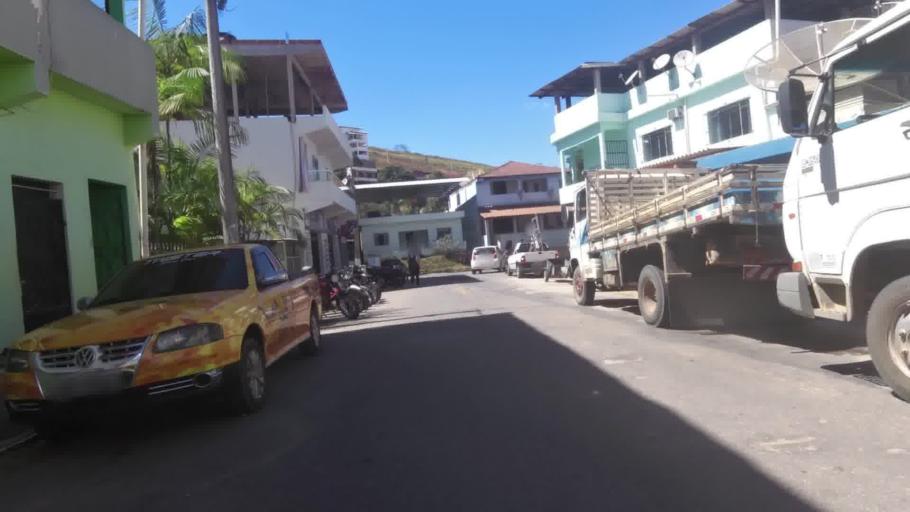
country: BR
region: Espirito Santo
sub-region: Cachoeiro De Itapemirim
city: Cachoeiro de Itapemirim
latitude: -20.9129
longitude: -41.1960
